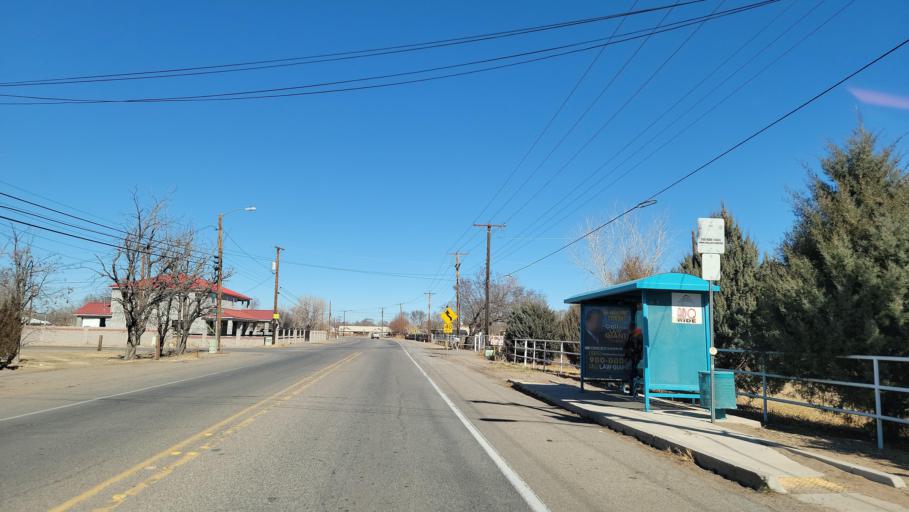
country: US
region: New Mexico
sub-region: Bernalillo County
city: South Valley
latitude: 34.9776
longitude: -106.6966
